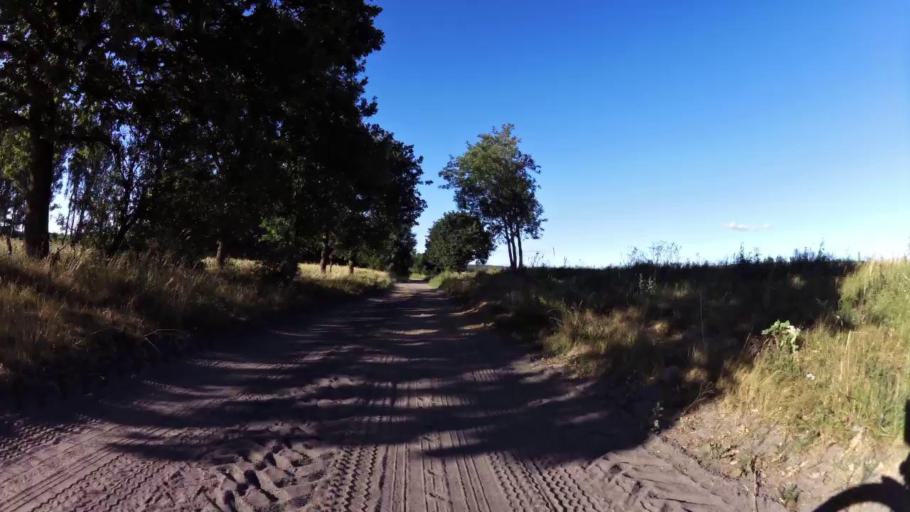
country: PL
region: West Pomeranian Voivodeship
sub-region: Powiat swidwinski
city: Swidwin
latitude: 53.7057
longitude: 15.8274
